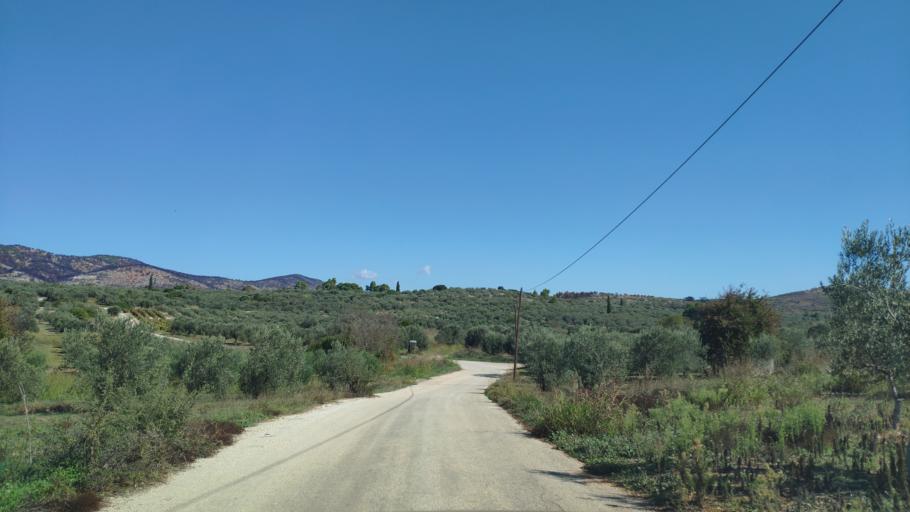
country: GR
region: Peloponnese
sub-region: Nomos Korinthias
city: Athikia
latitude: 37.8366
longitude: 22.9162
